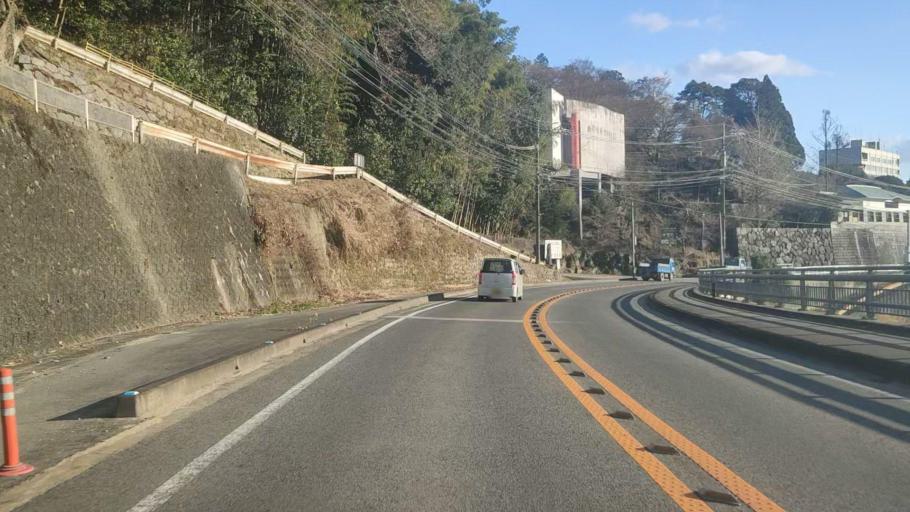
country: JP
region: Saga Prefecture
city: Saga-shi
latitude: 33.3305
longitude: 130.2679
